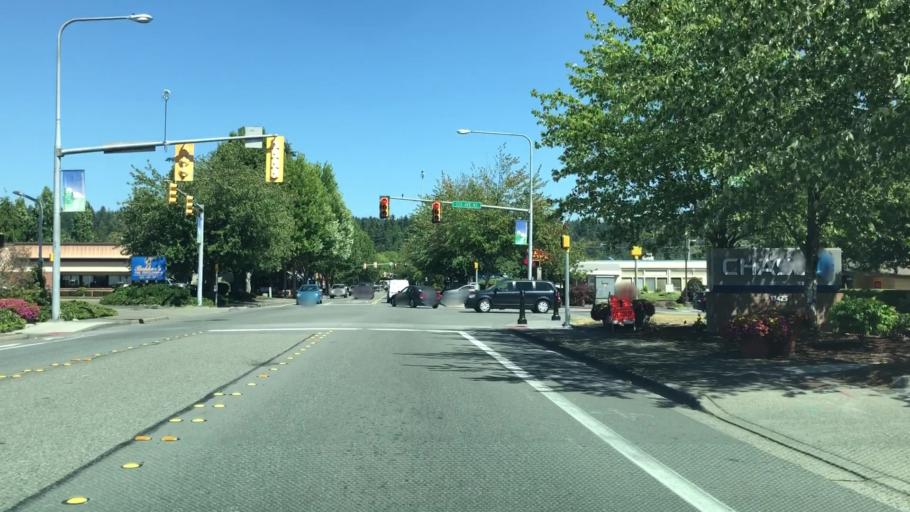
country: US
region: Washington
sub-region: King County
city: Woodinville
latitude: 47.7545
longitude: -122.1597
